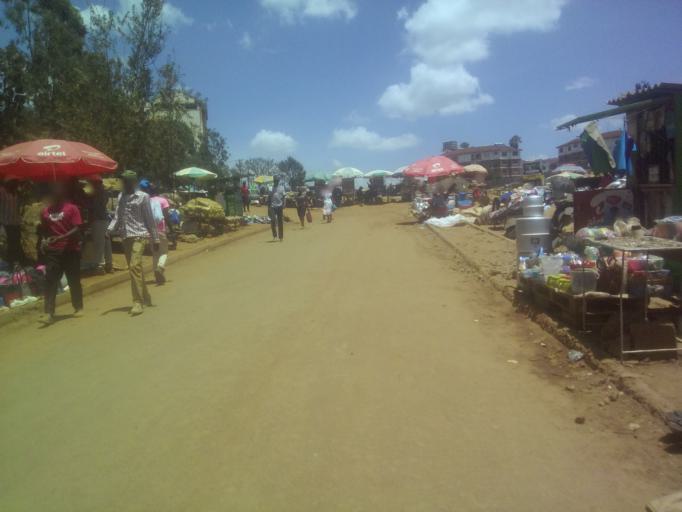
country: KE
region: Nairobi Area
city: Nairobi
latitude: -1.3050
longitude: 36.7880
